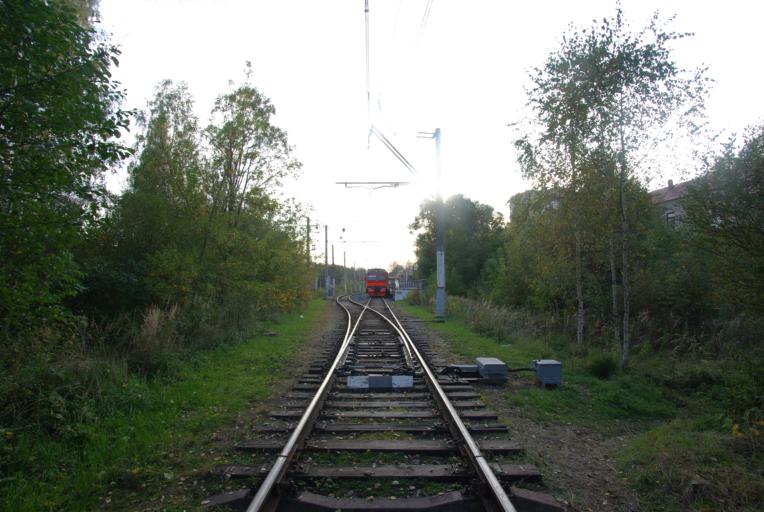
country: RU
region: Moskovskaya
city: Dubna
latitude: 56.7468
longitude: 37.2030
